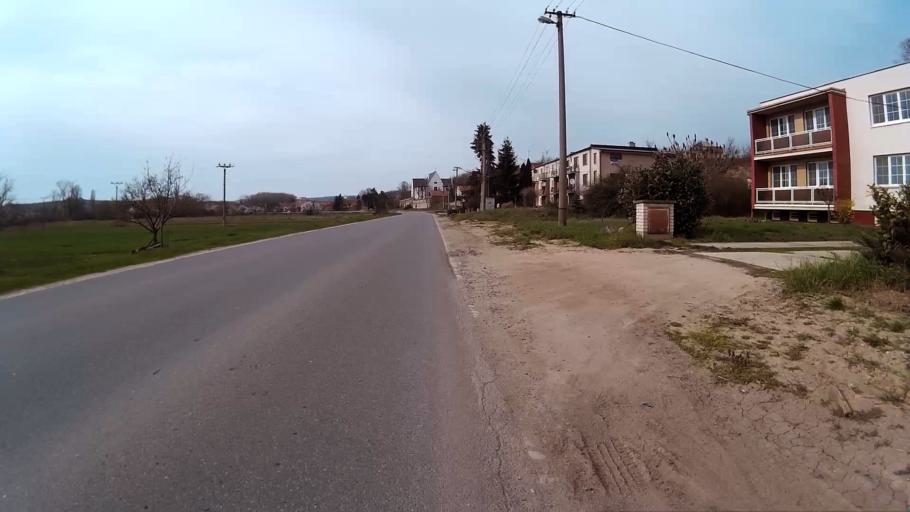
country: CZ
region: South Moravian
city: Dolni Kounice
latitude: 49.0519
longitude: 16.4912
